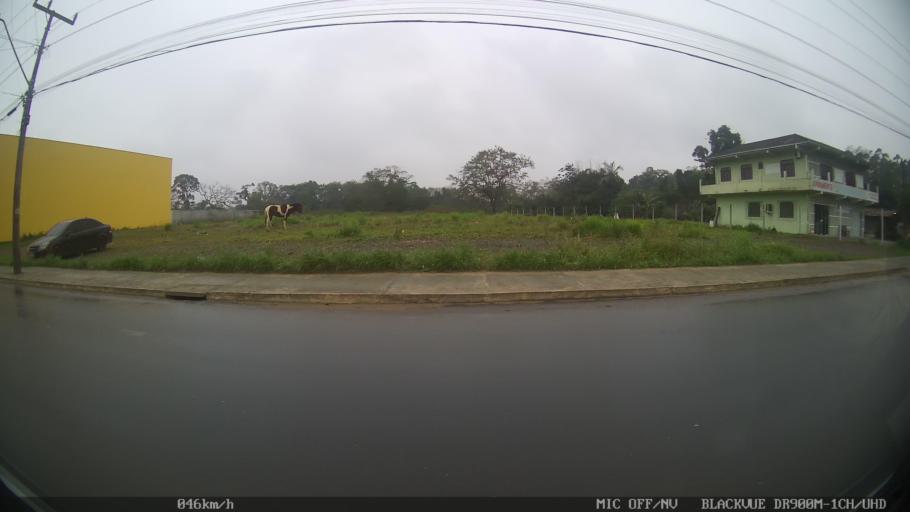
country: BR
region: Santa Catarina
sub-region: Joinville
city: Joinville
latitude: -26.2235
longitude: -48.8207
